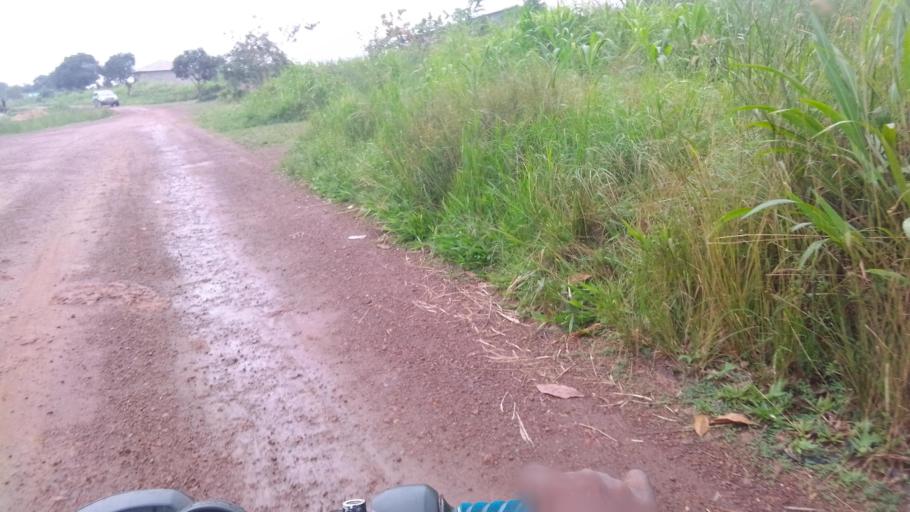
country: SL
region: Eastern Province
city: Kenema
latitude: 7.8979
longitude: -11.1719
